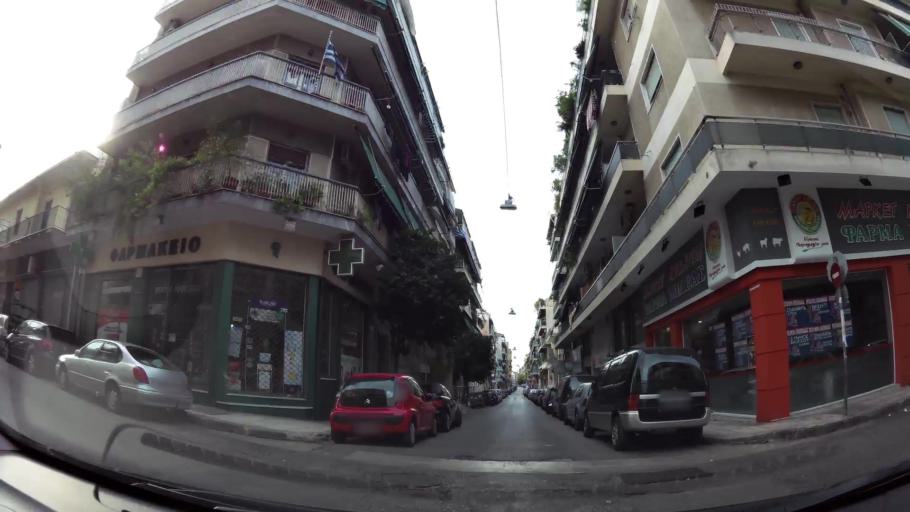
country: GR
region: Attica
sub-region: Nomarchia Athinas
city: Kipseli
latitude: 38.0103
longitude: 23.7257
